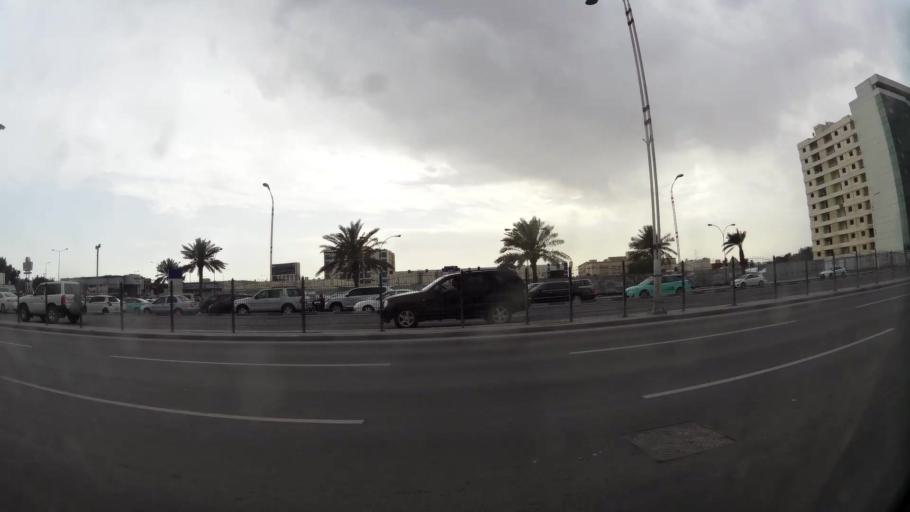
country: QA
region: Baladiyat ad Dawhah
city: Doha
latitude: 25.2733
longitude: 51.5102
